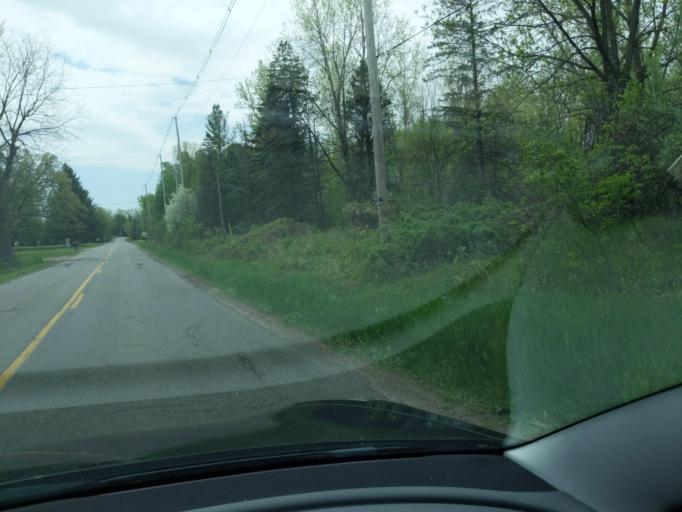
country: US
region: Michigan
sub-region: Ingham County
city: Holt
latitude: 42.6451
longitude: -84.5530
